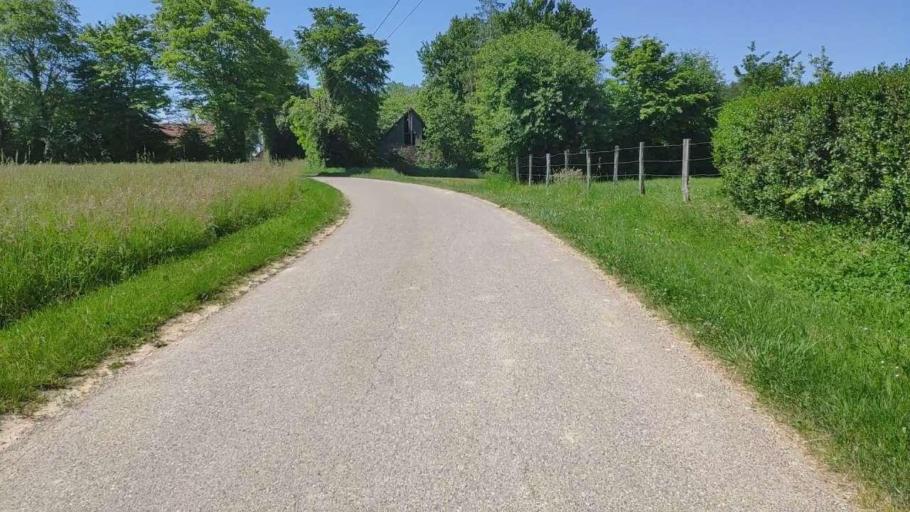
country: FR
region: Franche-Comte
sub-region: Departement du Jura
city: Bletterans
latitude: 46.7760
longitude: 5.4139
